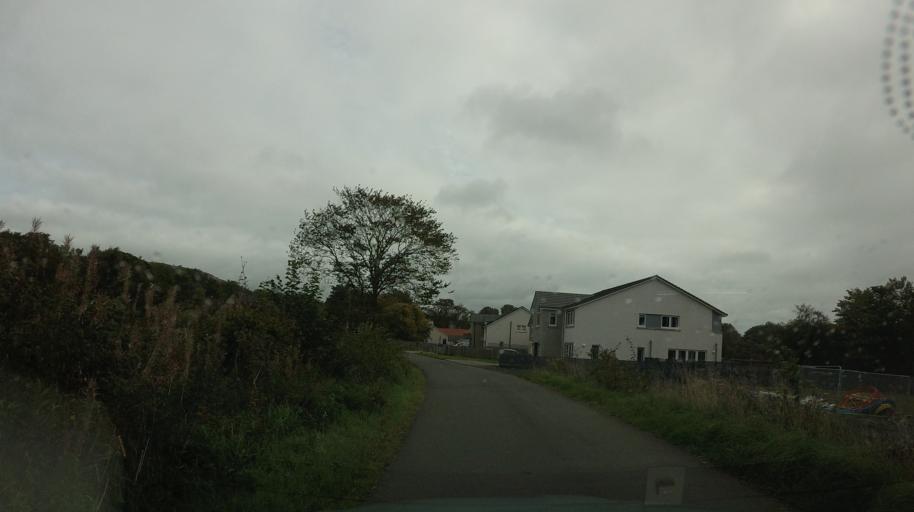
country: GB
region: Scotland
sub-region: Fife
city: Kelty
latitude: 56.1475
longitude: -3.3751
